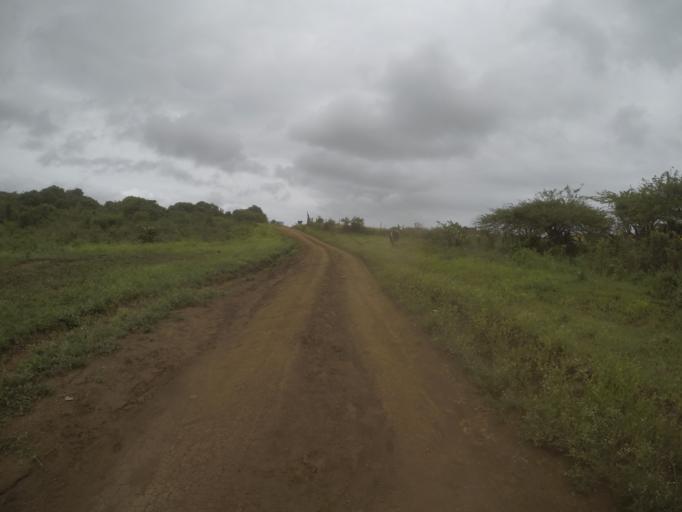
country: ZA
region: KwaZulu-Natal
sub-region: uThungulu District Municipality
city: Empangeni
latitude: -28.6026
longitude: 31.8455
